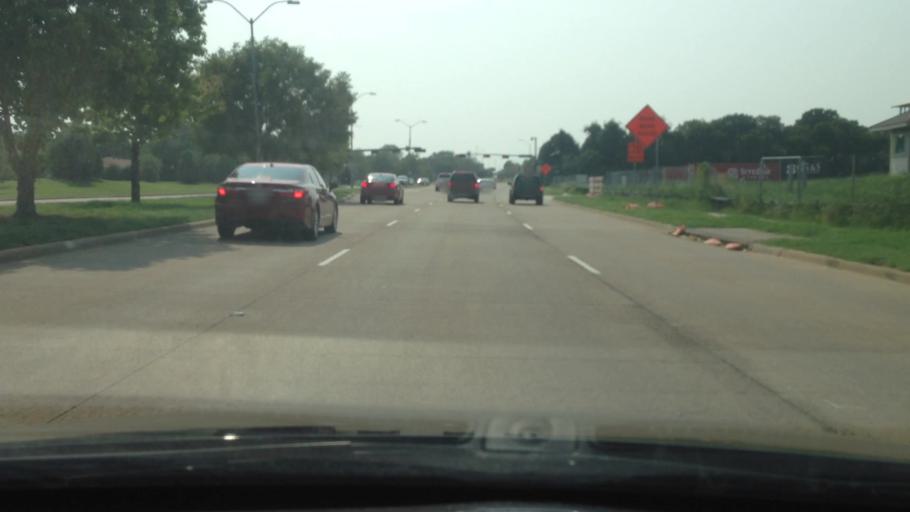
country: US
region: Texas
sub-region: Tarrant County
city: North Richland Hills
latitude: 32.8618
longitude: -97.2014
